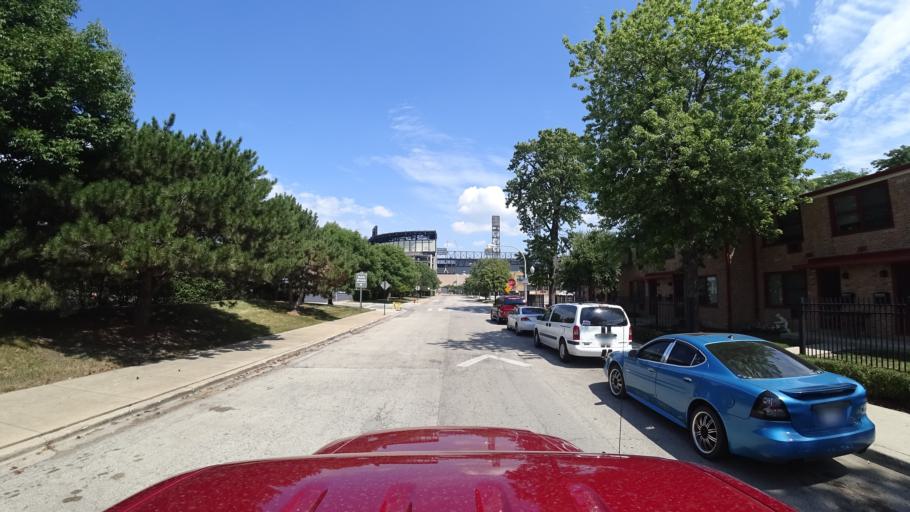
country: US
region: Illinois
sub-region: Cook County
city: Chicago
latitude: 41.8268
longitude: -87.6338
